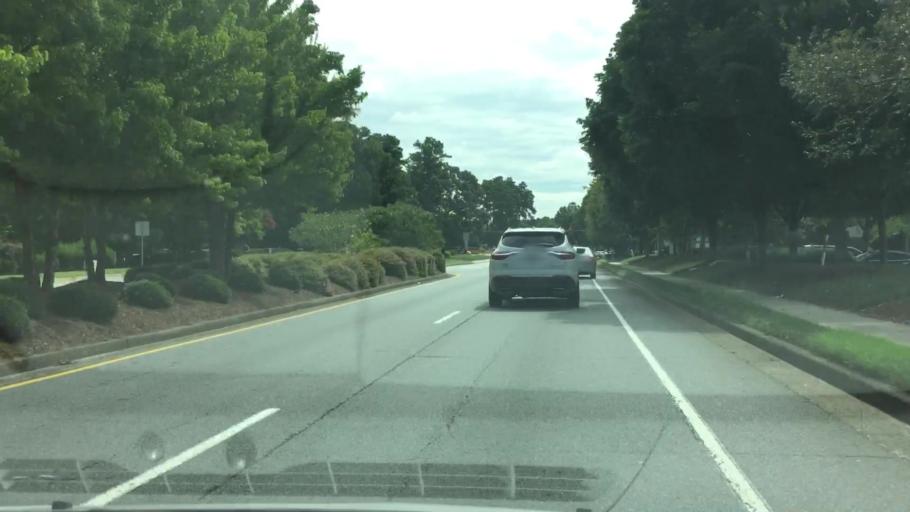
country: US
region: Georgia
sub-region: Fulton County
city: Alpharetta
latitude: 34.0884
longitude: -84.2723
